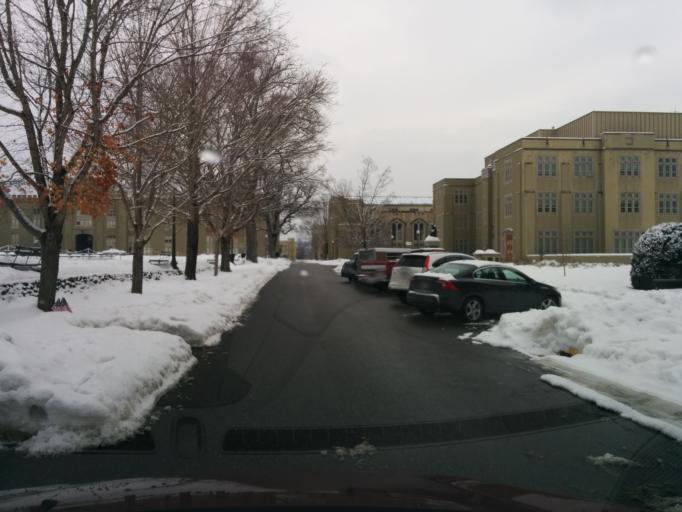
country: US
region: Virginia
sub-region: City of Lexington
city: Lexington
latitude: 37.7899
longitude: -79.4373
